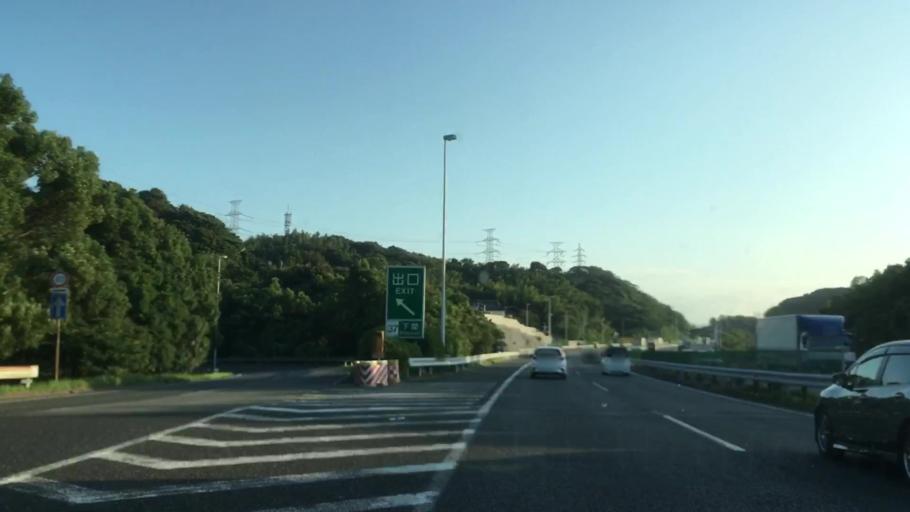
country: JP
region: Yamaguchi
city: Shimonoseki
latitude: 33.9786
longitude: 130.9525
